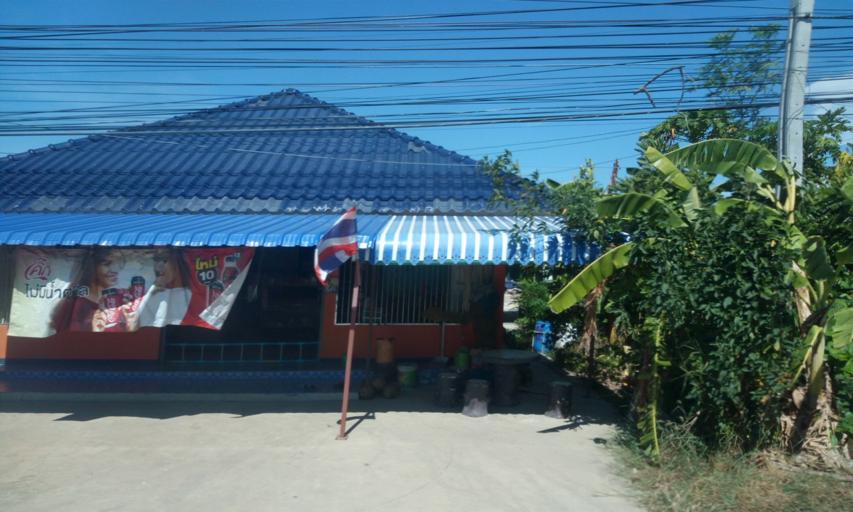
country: TH
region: Samut Prakan
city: Bang Bo District
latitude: 13.5206
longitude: 100.7885
